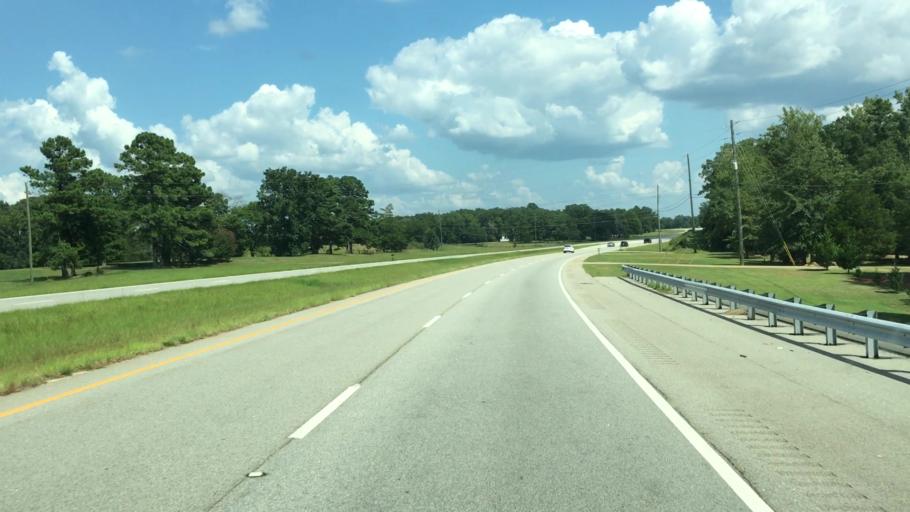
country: US
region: Georgia
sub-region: Putnam County
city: Eatonton
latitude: 33.2725
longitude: -83.3498
